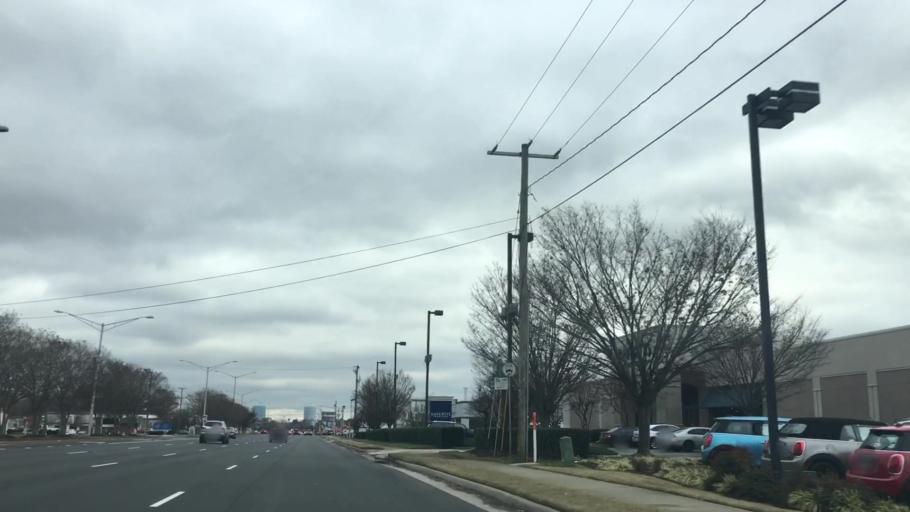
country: US
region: Virginia
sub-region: City of Chesapeake
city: Chesapeake
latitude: 36.8472
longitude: -76.1607
